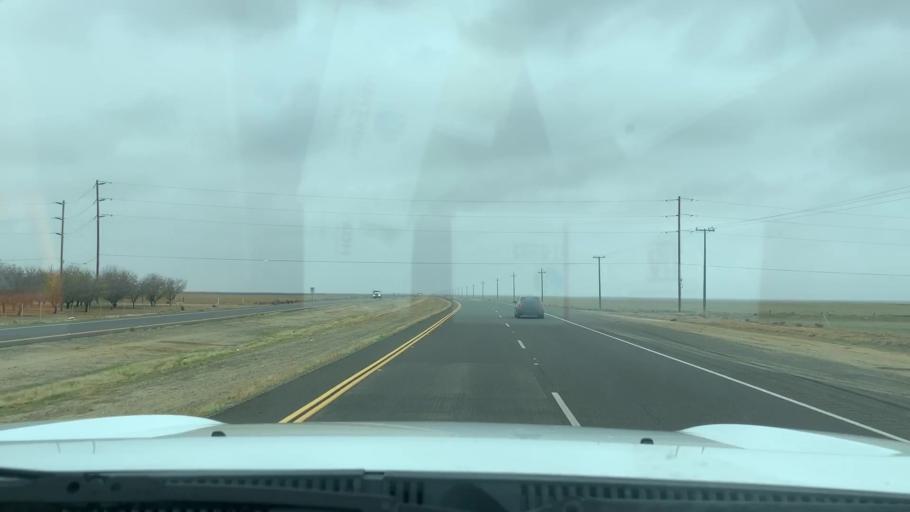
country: US
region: California
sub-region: Kern County
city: Lost Hills
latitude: 35.6159
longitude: -119.7596
